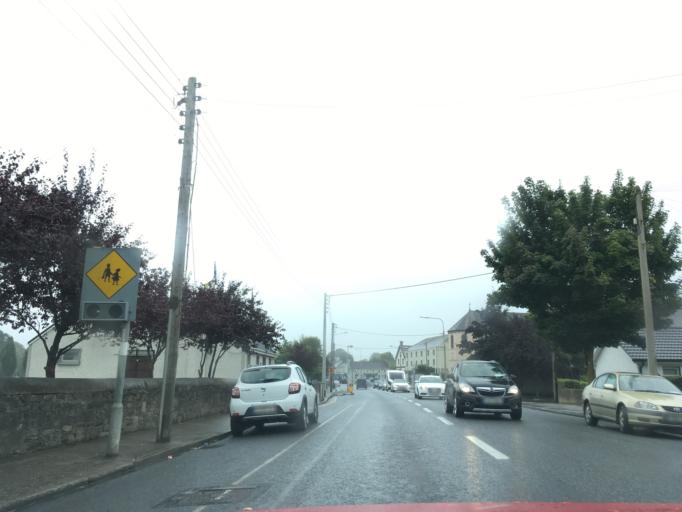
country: IE
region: Munster
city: Carrick-on-Suir
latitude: 52.3485
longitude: -7.4127
